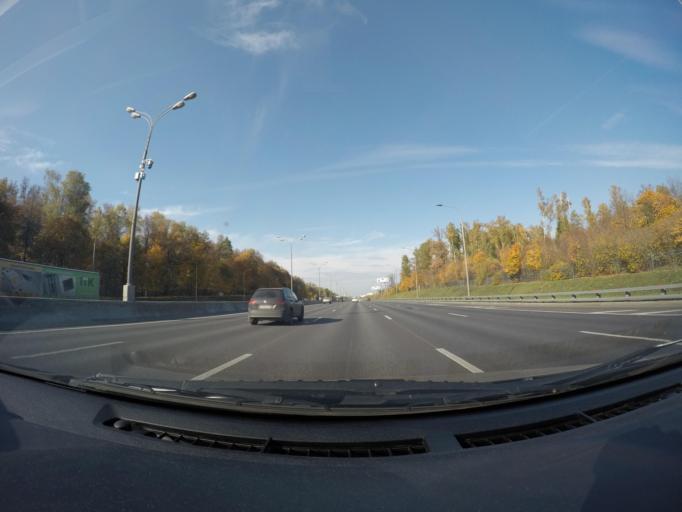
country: RU
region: Moskovskaya
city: Druzhba
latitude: 55.8583
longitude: 37.7733
